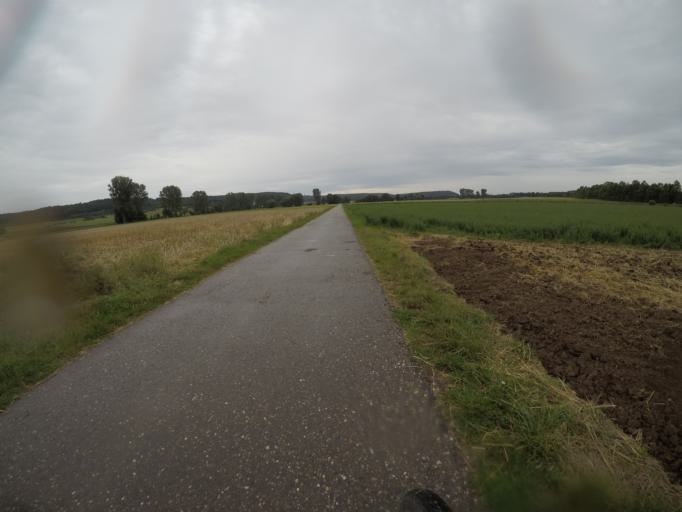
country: DE
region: Baden-Wuerttemberg
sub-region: Regierungsbezirk Stuttgart
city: Ehningen
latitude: 48.6385
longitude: 8.9308
